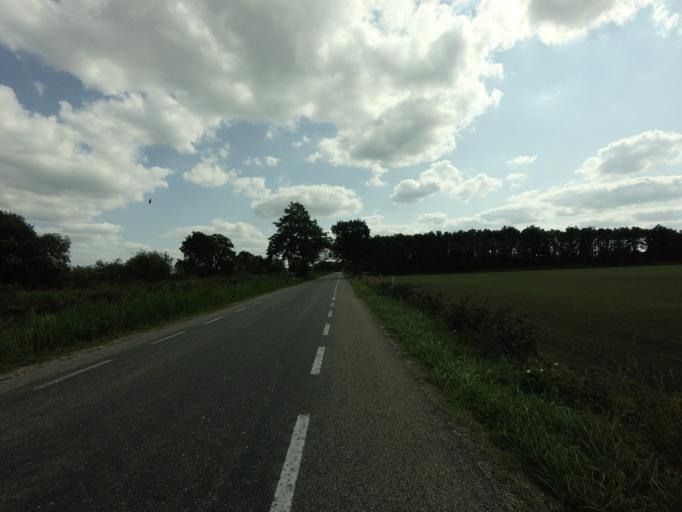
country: NL
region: Drenthe
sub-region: Gemeente Westerveld
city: Dwingeloo
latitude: 52.8753
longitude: 6.4349
